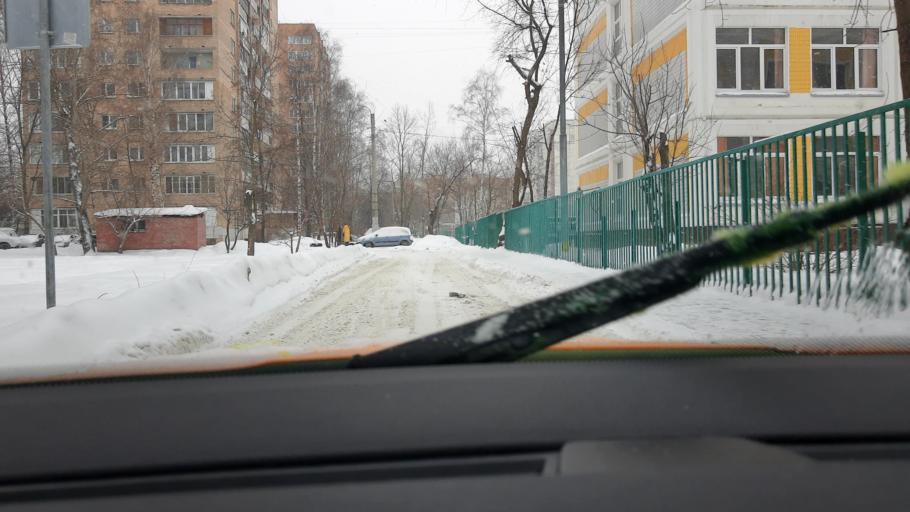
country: RU
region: Moscow
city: Vatutino
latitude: 55.8724
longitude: 37.6713
